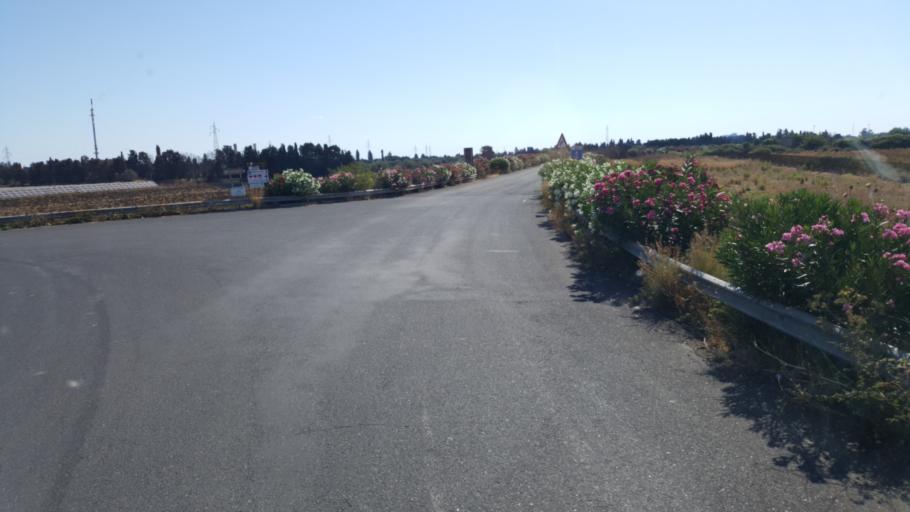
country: IT
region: Sicily
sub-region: Provincia di Siracusa
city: Melilli
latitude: 37.2016
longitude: 15.1639
